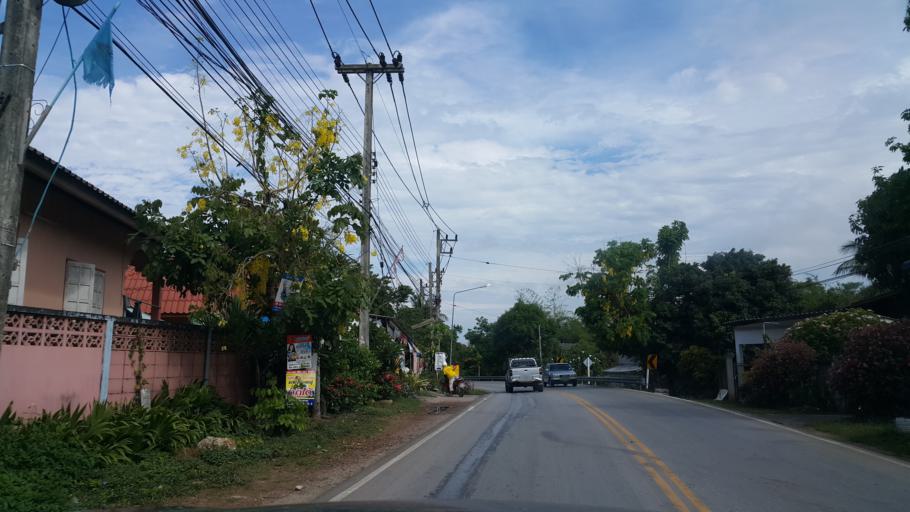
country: TH
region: Chiang Rai
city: Chiang Rai
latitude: 19.9113
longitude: 99.8773
